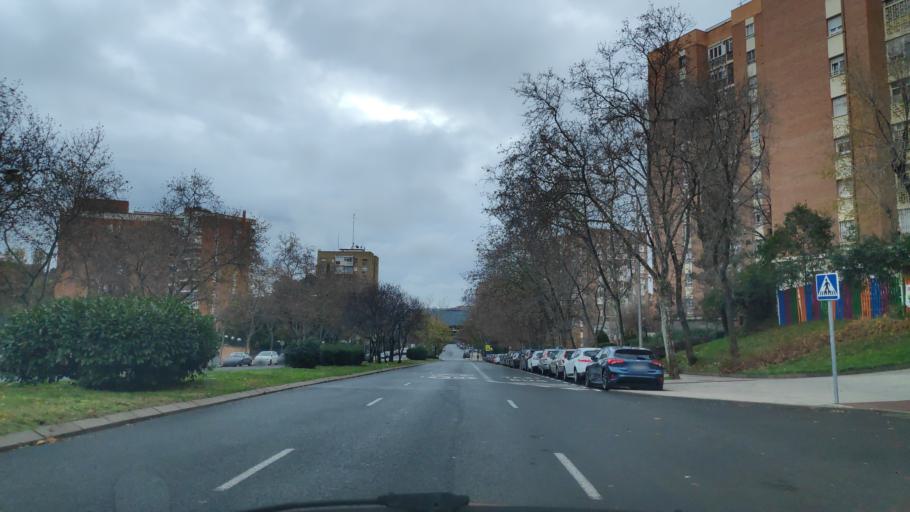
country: ES
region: Madrid
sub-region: Provincia de Madrid
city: Hortaleza
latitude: 40.4724
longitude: -3.6482
